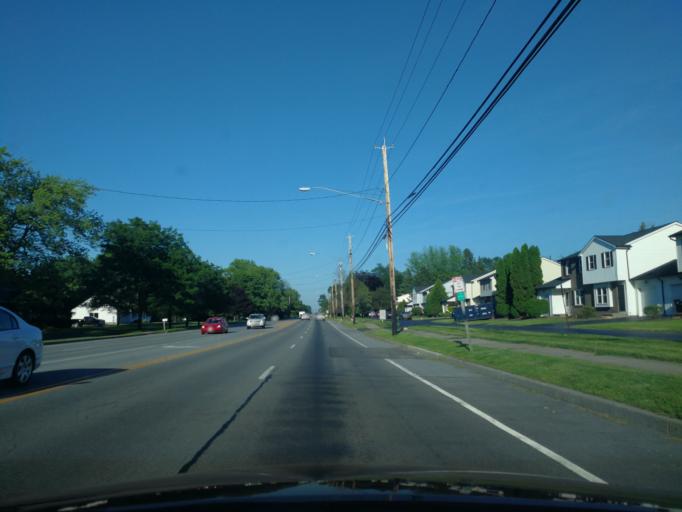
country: US
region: New York
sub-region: Monroe County
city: Greece
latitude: 43.2532
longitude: -77.7148
